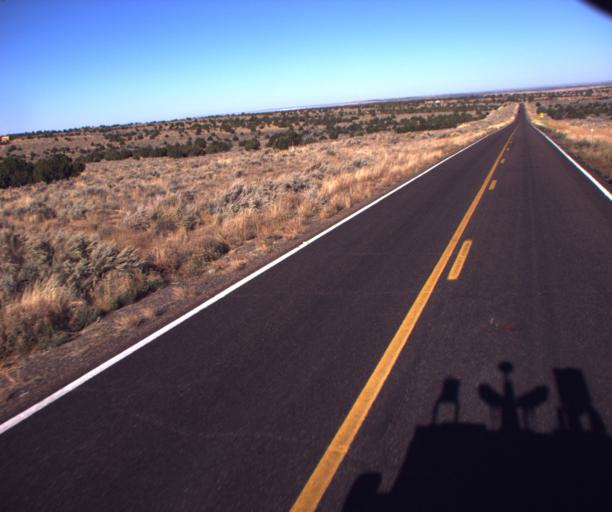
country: US
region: Arizona
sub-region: Navajo County
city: First Mesa
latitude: 35.7953
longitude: -110.1891
